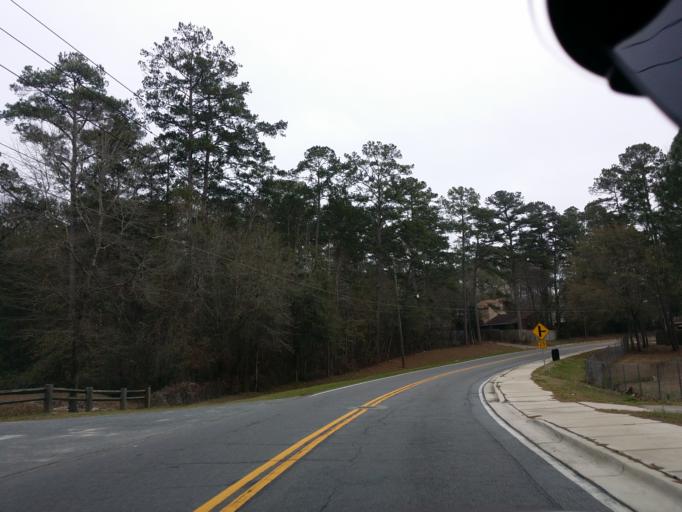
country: US
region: Florida
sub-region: Leon County
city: Tallahassee
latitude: 30.4790
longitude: -84.2207
